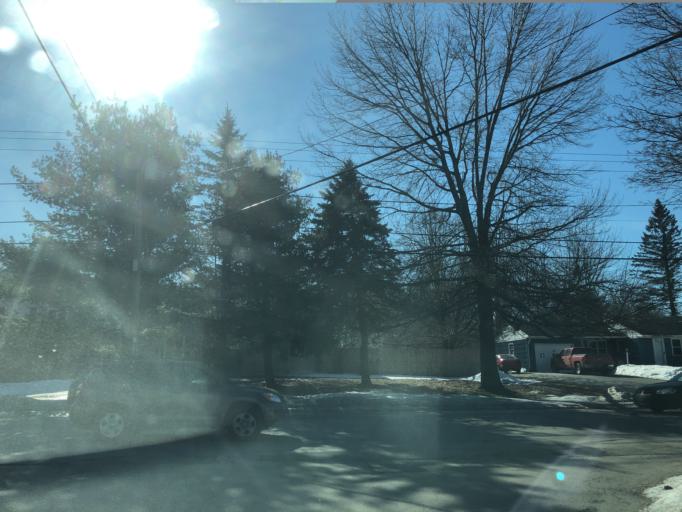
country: US
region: Maine
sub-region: Penobscot County
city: Brewer
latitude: 44.8187
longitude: -68.7495
